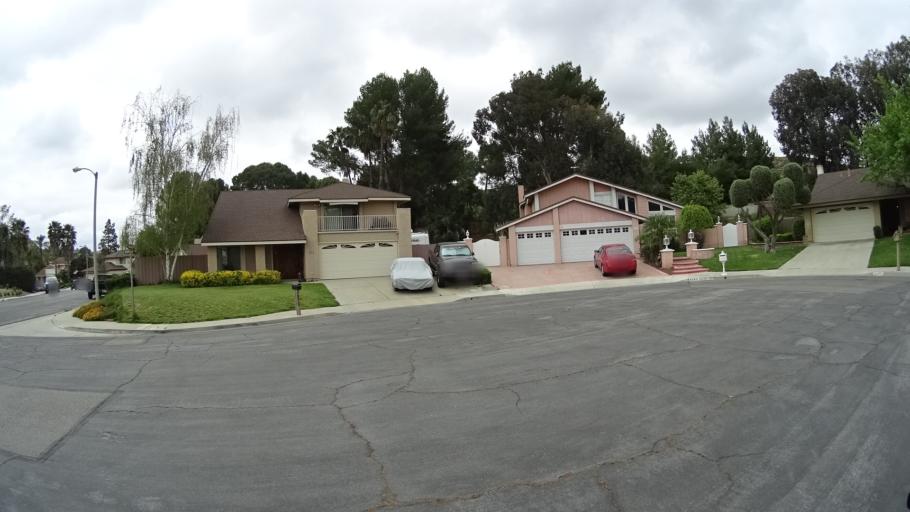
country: US
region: California
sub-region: Ventura County
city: Moorpark
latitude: 34.2217
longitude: -118.8900
